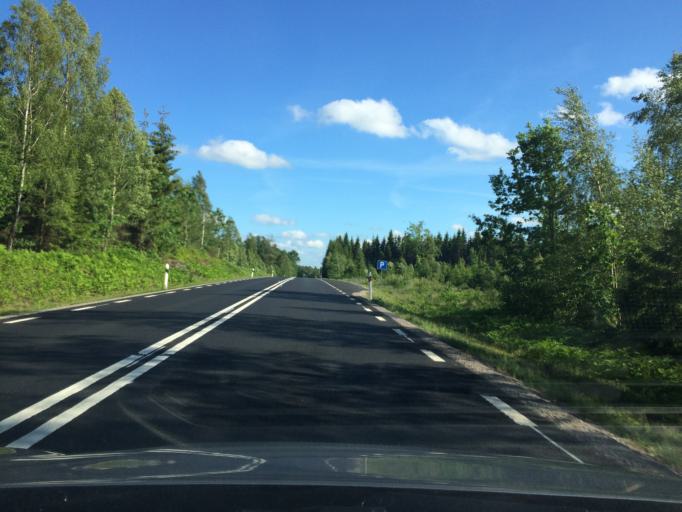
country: SE
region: Kronoberg
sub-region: Alvesta Kommun
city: Moheda
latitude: 57.0080
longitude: 14.6617
